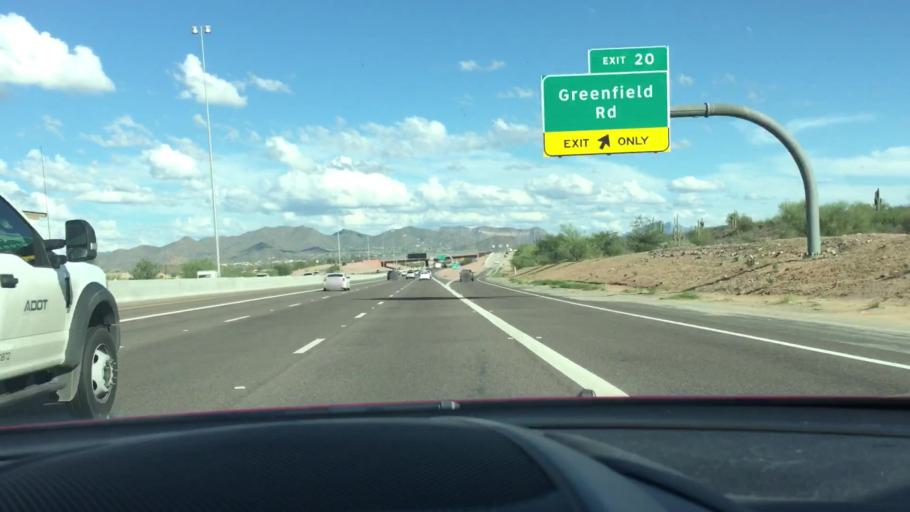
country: US
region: Arizona
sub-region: Maricopa County
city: Mesa
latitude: 33.4800
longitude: -111.7426
